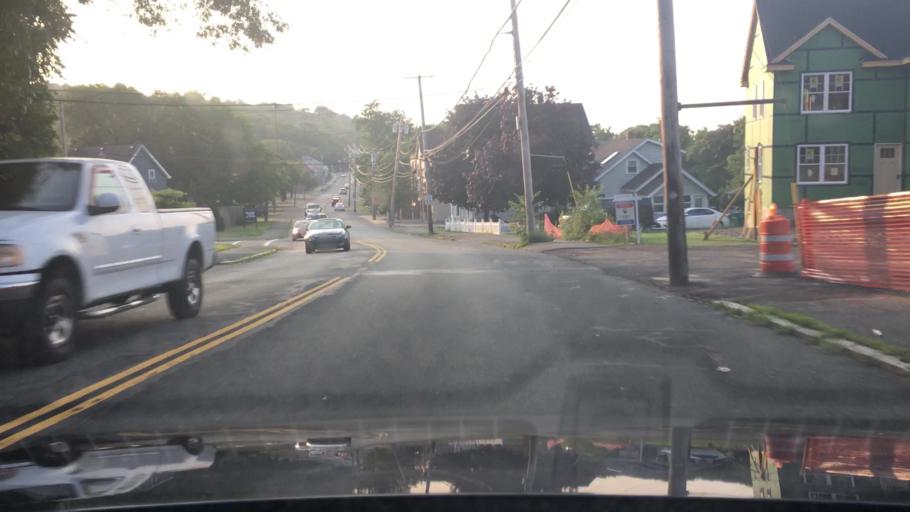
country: US
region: Massachusetts
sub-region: Essex County
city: Saugus
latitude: 42.4719
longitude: -70.9826
